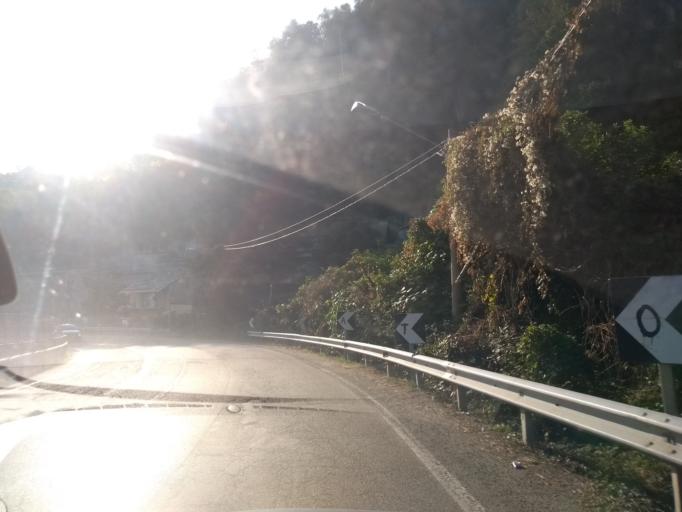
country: IT
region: Piedmont
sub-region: Provincia di Torino
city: Lanzo Torinese
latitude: 45.2682
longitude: 7.4861
